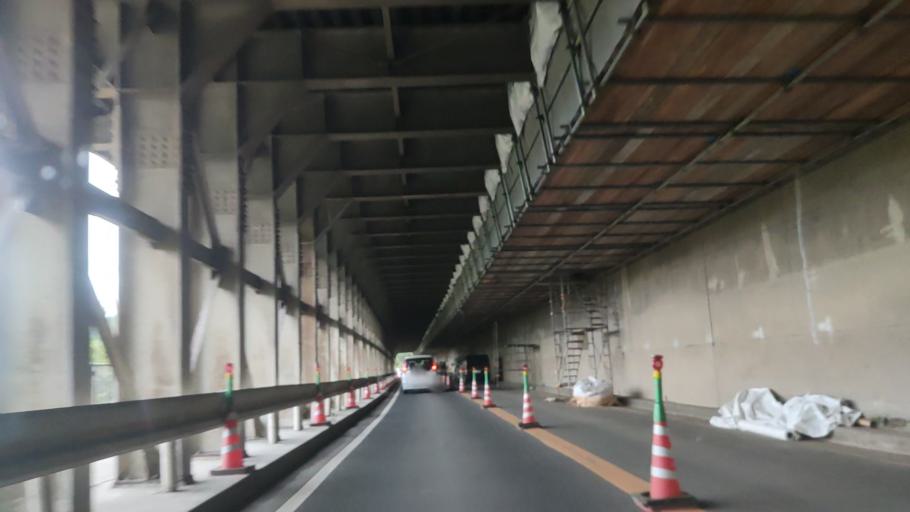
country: JP
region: Hyogo
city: Toyooka
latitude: 35.4511
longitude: 134.7729
